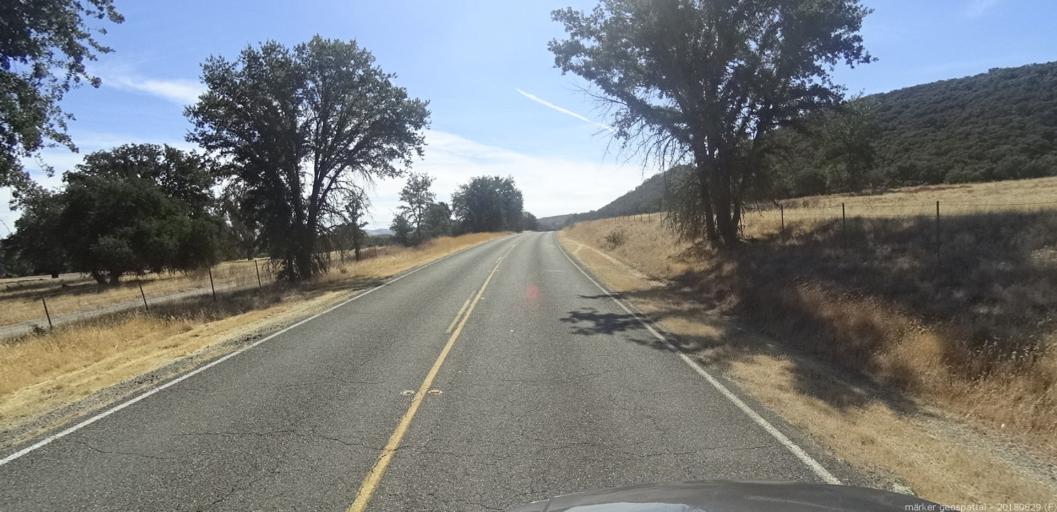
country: US
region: California
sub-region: San Luis Obispo County
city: Lake Nacimiento
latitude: 35.8902
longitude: -121.0770
